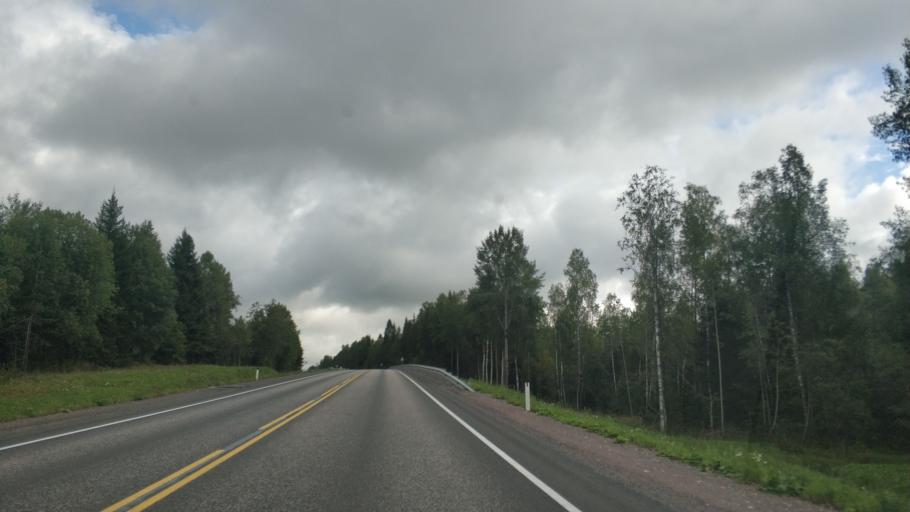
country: RU
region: Republic of Karelia
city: Khelyulya
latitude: 61.8376
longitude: 30.6430
